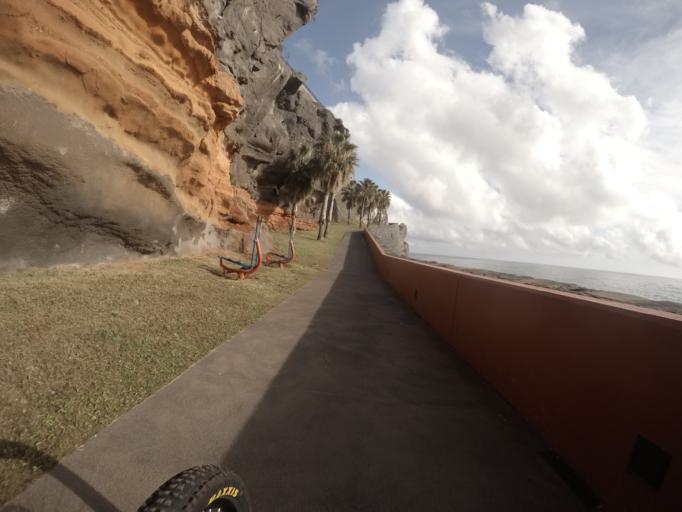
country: PT
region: Madeira
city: Camara de Lobos
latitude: 32.6457
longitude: -16.9724
